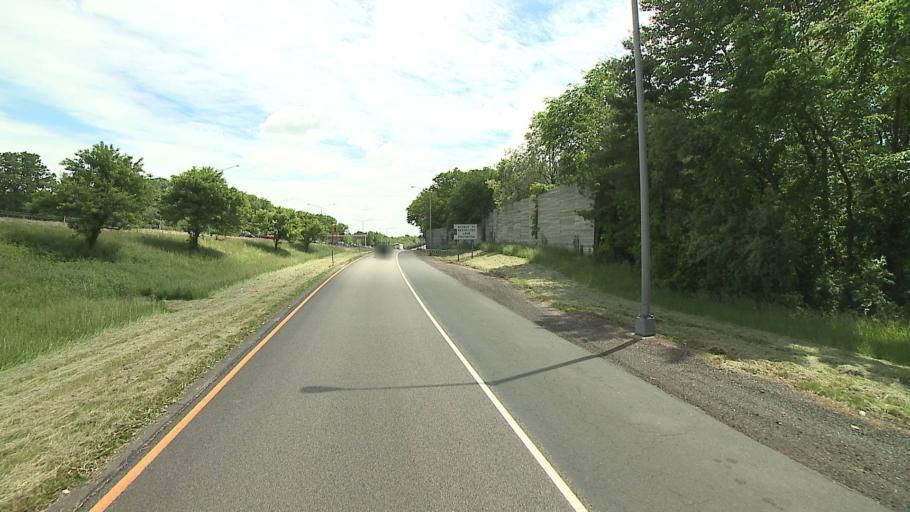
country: US
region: Connecticut
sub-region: Hartford County
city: Windsor
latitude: 41.8372
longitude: -72.6659
